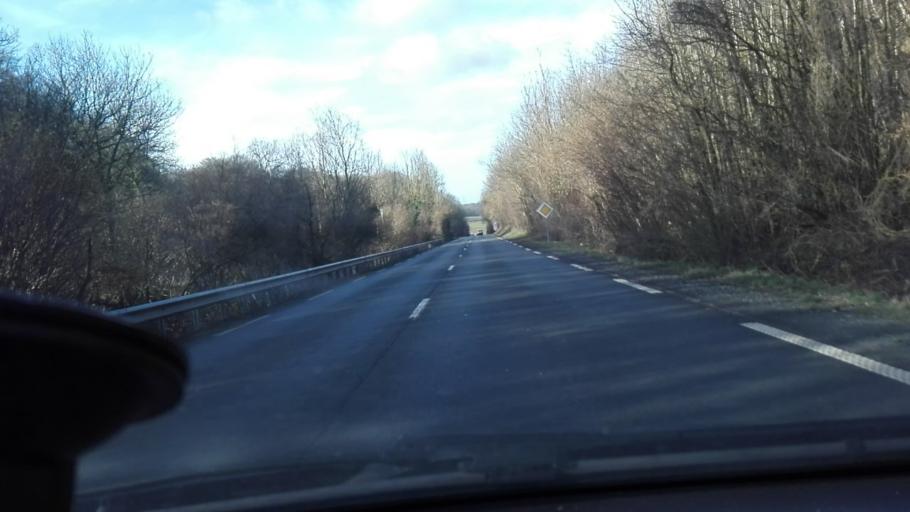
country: FR
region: Nord-Pas-de-Calais
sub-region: Departement du Pas-de-Calais
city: Licques
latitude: 50.7148
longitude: 1.9631
